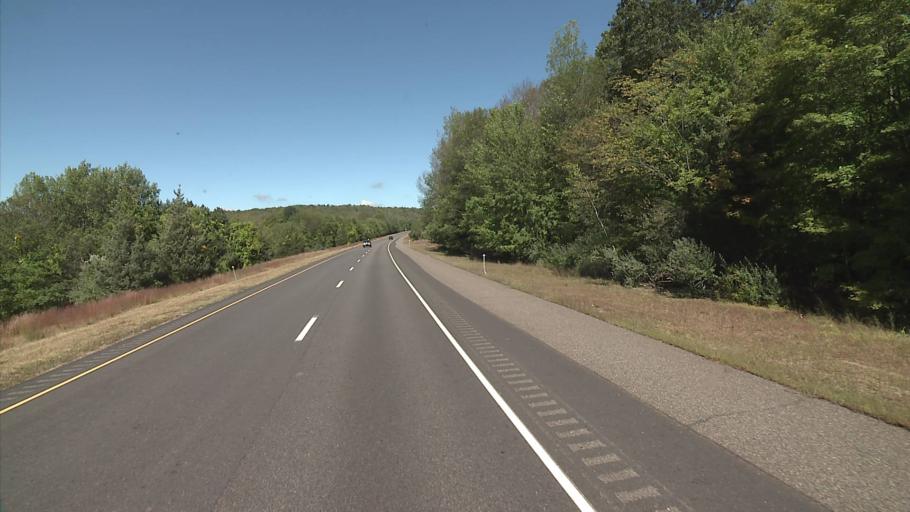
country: US
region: Connecticut
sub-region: New London County
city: Colchester
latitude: 41.4758
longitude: -72.2942
